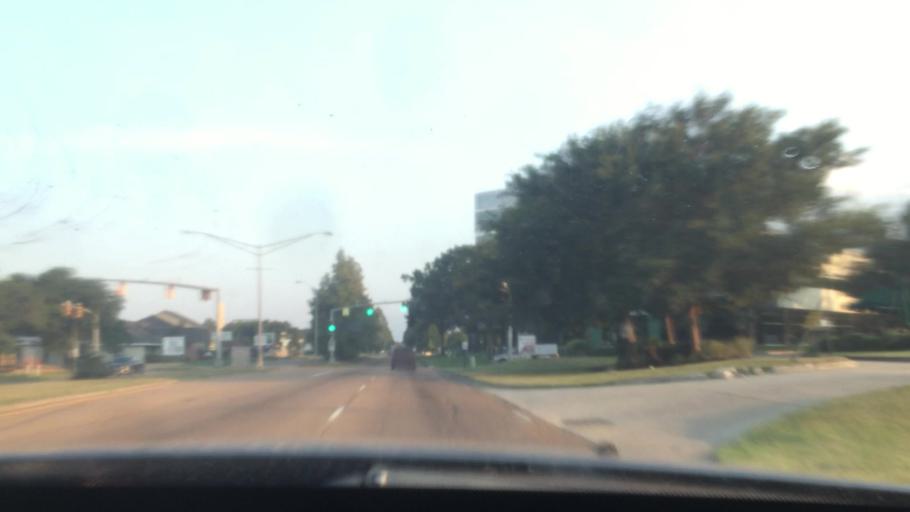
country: US
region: Louisiana
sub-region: East Baton Rouge Parish
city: Inniswold
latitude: 30.4181
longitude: -91.0517
